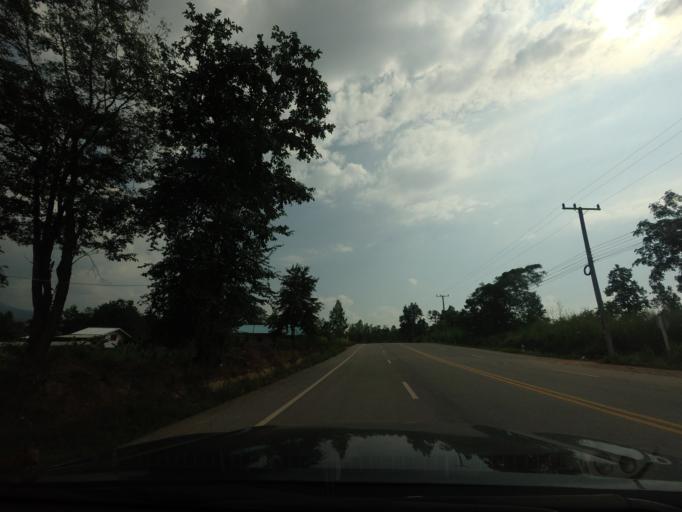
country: TH
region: Phitsanulok
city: Nakhon Thai
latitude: 17.0271
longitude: 100.9122
